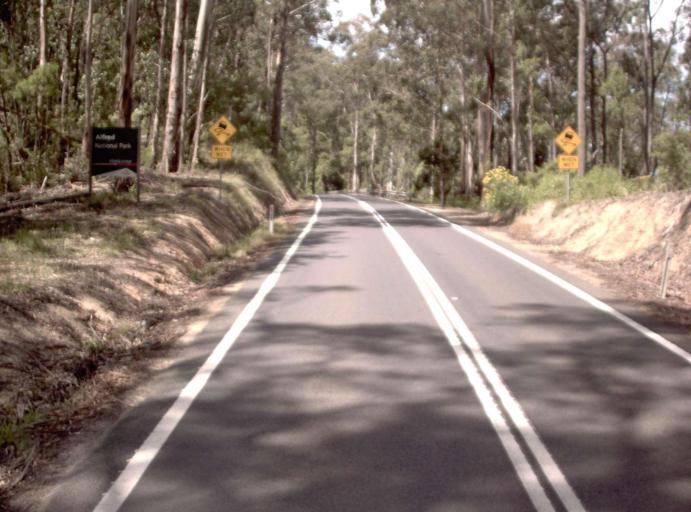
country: AU
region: New South Wales
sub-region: Bombala
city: Bombala
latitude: -37.5633
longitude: 149.3470
